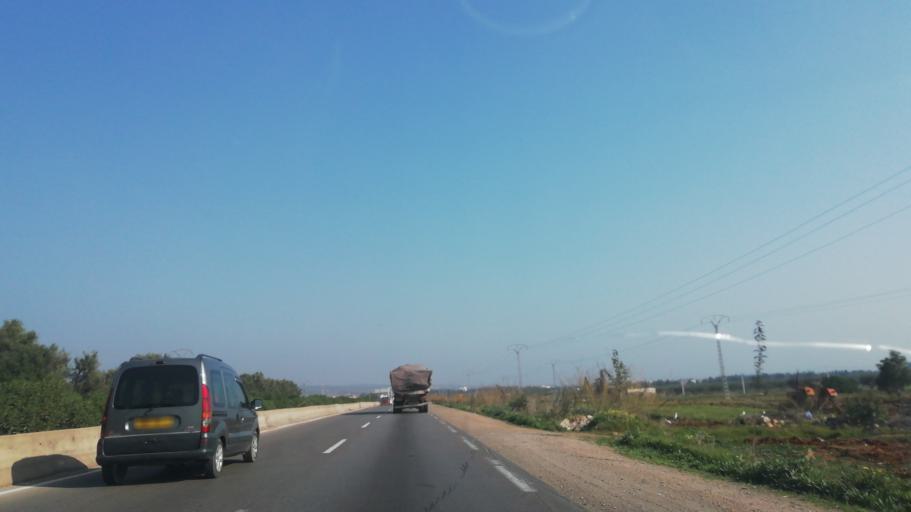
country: DZ
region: Oran
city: Bou Tlelis
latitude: 35.5651
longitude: -0.9200
